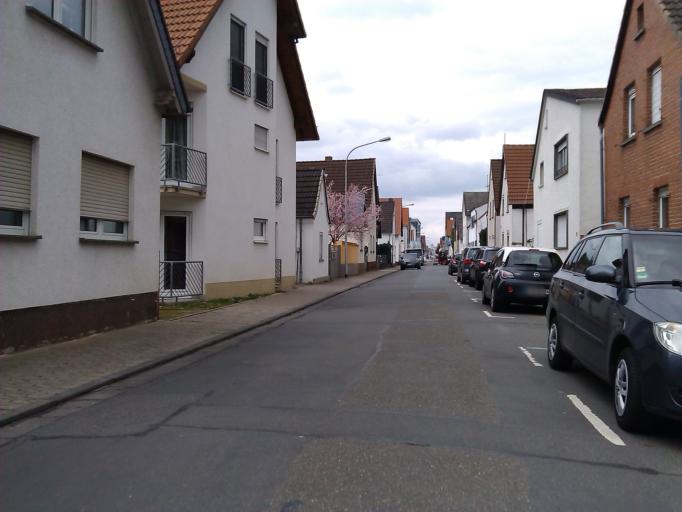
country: DE
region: Hesse
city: Griesheim
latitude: 49.8580
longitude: 8.5586
